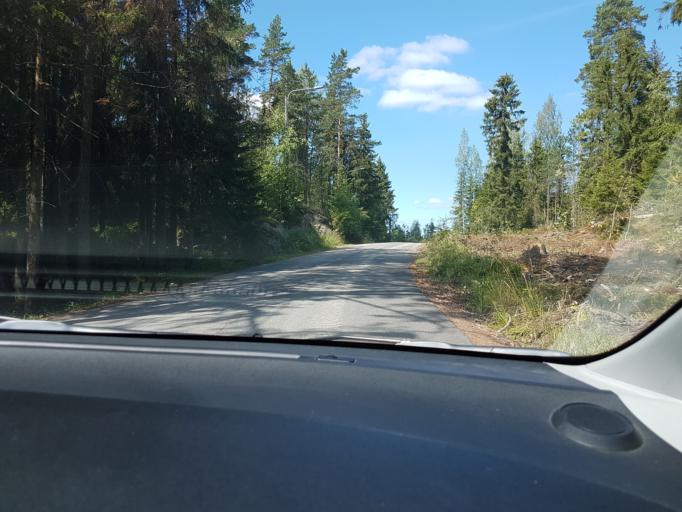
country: FI
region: Uusimaa
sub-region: Helsinki
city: Kilo
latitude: 60.3279
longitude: 24.7647
